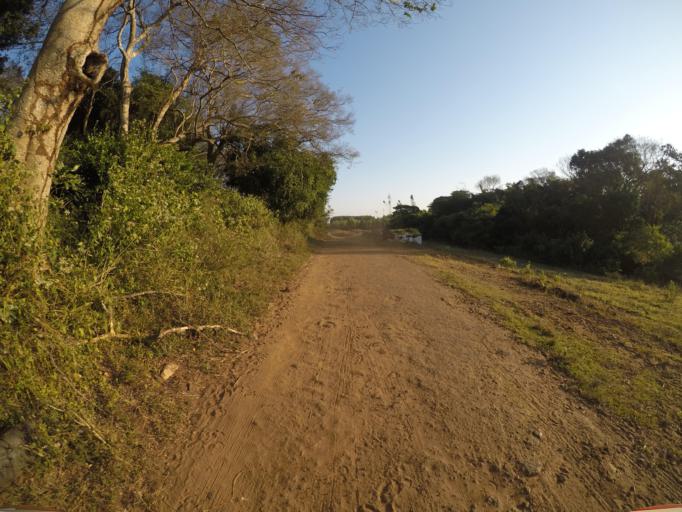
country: ZA
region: KwaZulu-Natal
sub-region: uThungulu District Municipality
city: KwaMbonambi
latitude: -28.6940
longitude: 32.1984
